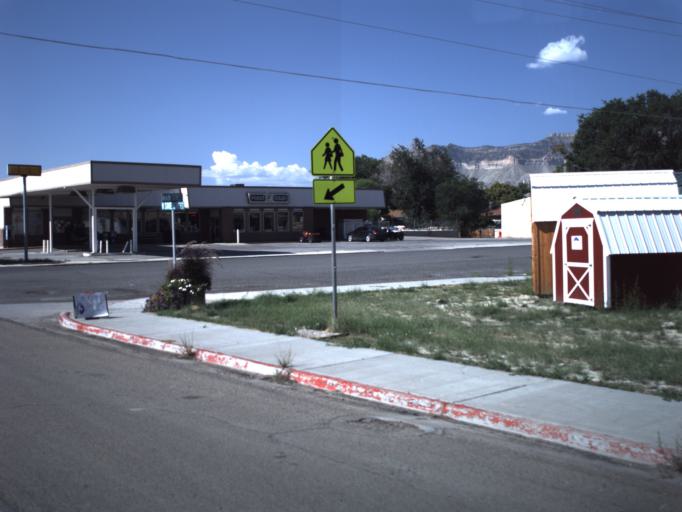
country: US
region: Utah
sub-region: Emery County
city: Ferron
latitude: 39.0903
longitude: -111.1321
